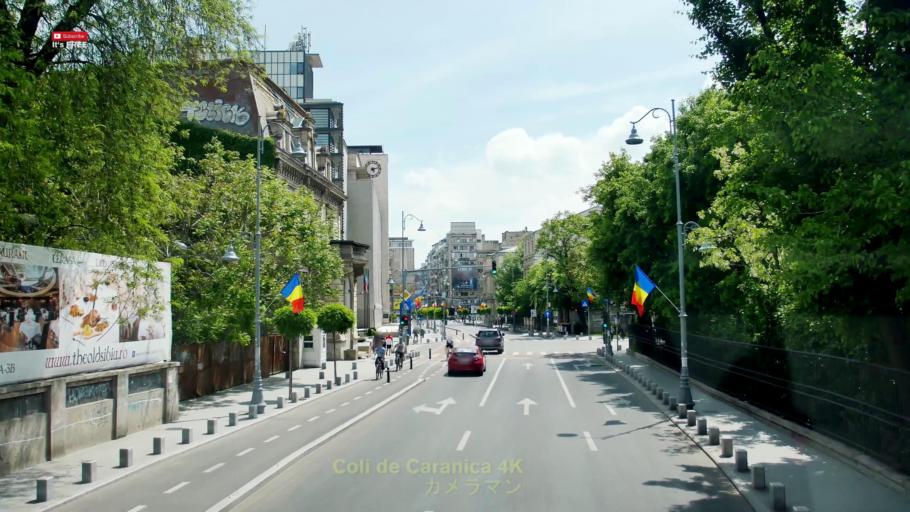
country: RO
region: Bucuresti
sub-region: Municipiul Bucuresti
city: Bucuresti
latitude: 44.4462
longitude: 26.0905
